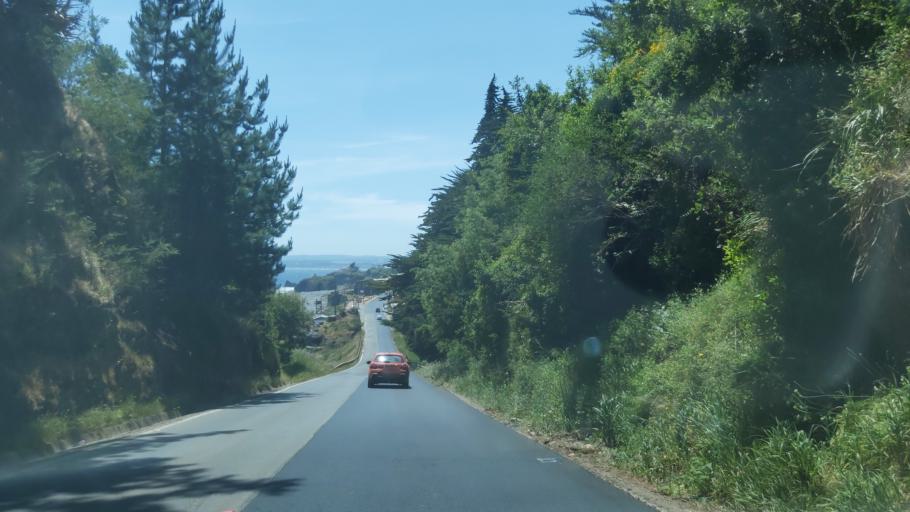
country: CL
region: Maule
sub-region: Provincia de Cauquenes
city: Cauquenes
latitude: -35.8235
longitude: -72.6015
